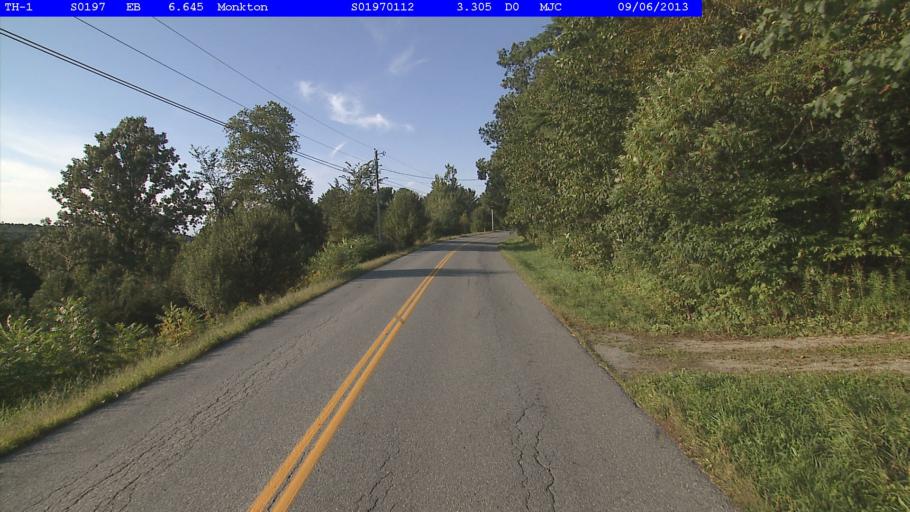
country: US
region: Vermont
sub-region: Chittenden County
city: Hinesburg
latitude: 44.2249
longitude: -73.1534
